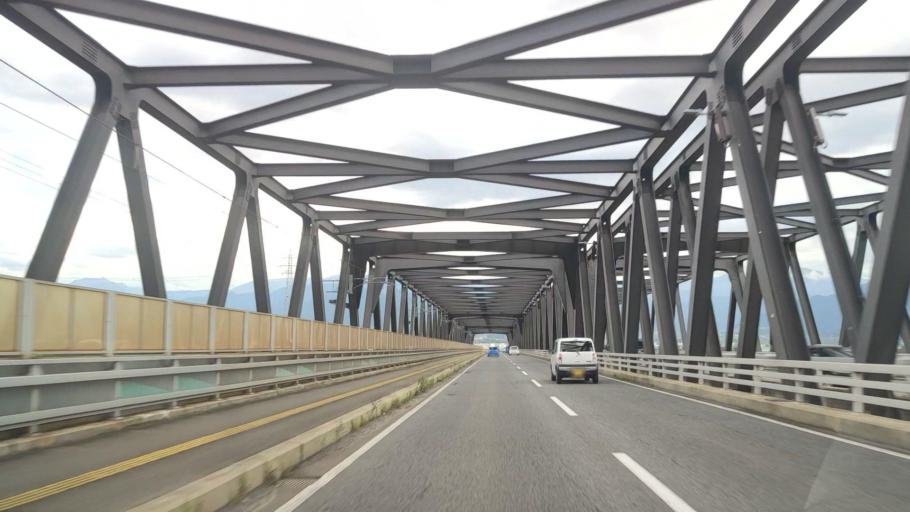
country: JP
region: Nagano
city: Suzaka
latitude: 36.6632
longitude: 138.2690
